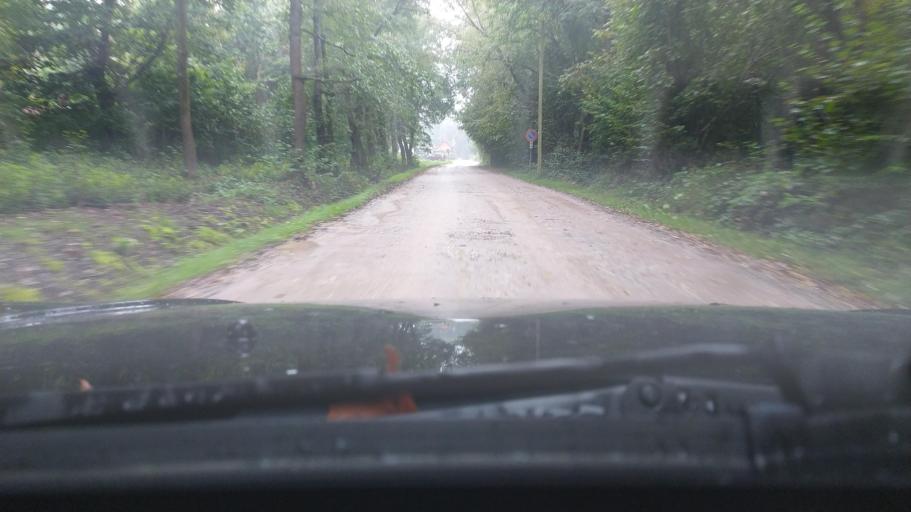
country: IT
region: Lombardy
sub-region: Provincia di Varese
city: Angera
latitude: 45.7621
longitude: 8.5858
